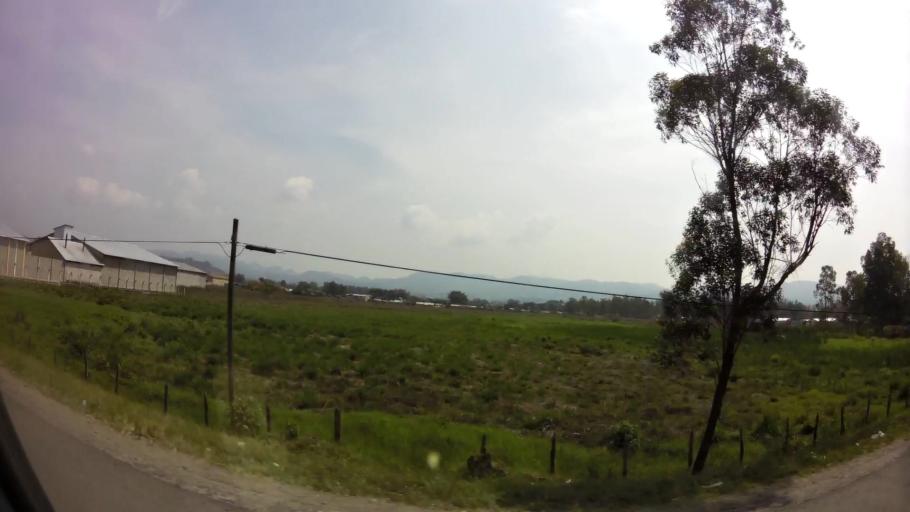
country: HN
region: Comayagua
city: Siguatepeque
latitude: 14.5812
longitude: -87.8426
